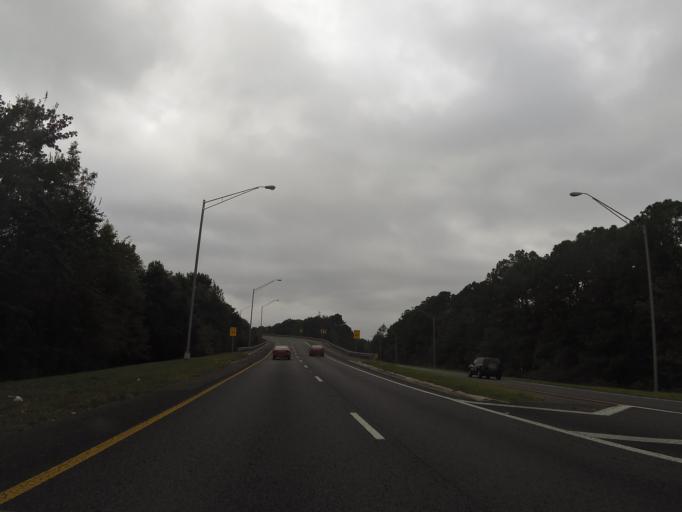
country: US
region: Florida
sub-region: Duval County
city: Jacksonville
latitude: 30.3163
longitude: -81.7659
